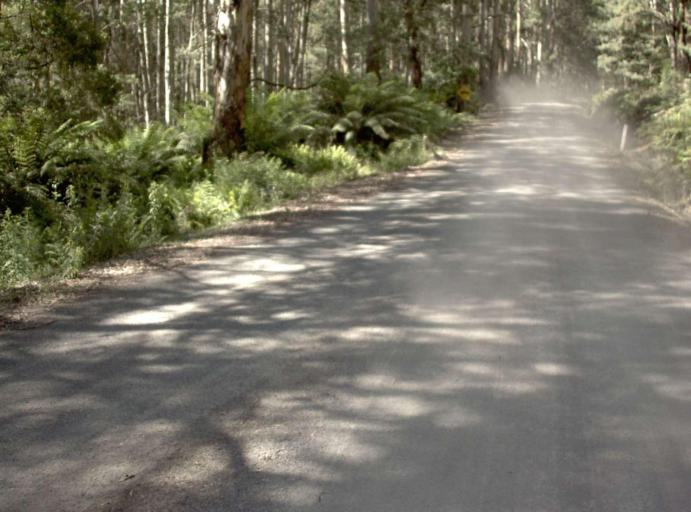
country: AU
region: New South Wales
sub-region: Bombala
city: Bombala
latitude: -37.2433
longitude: 148.7575
